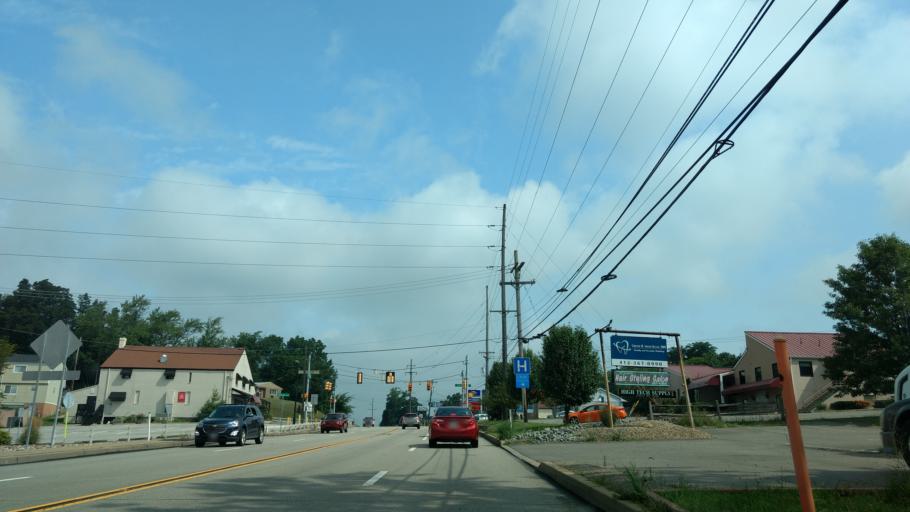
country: US
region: Pennsylvania
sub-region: Allegheny County
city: West View
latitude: 40.5711
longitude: -80.0371
